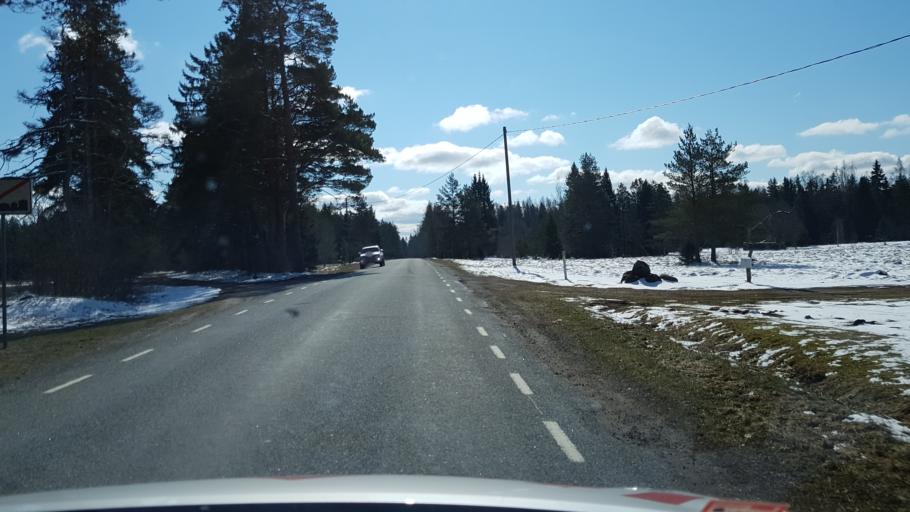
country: EE
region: Laeaene-Virumaa
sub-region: Tapa vald
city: Tapa
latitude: 59.5035
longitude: 25.9657
